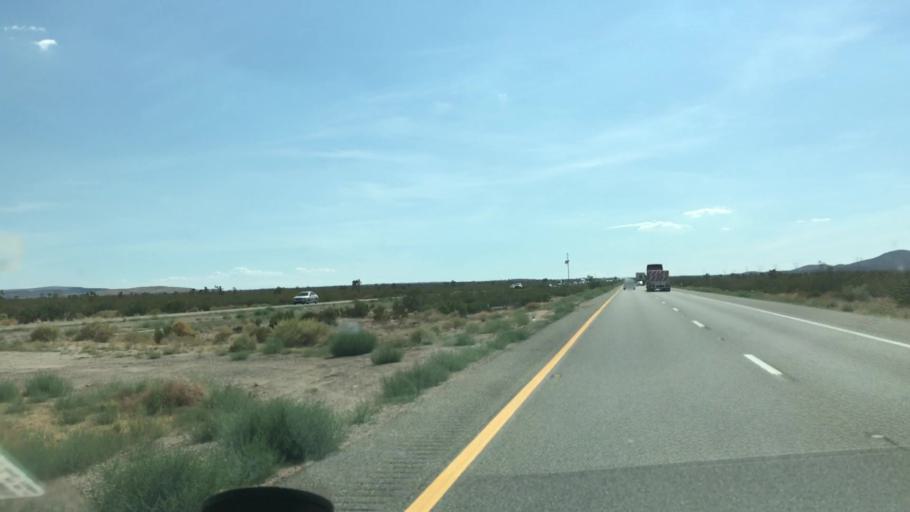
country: US
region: Nevada
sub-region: Clark County
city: Sandy Valley
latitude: 35.4208
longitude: -115.7408
